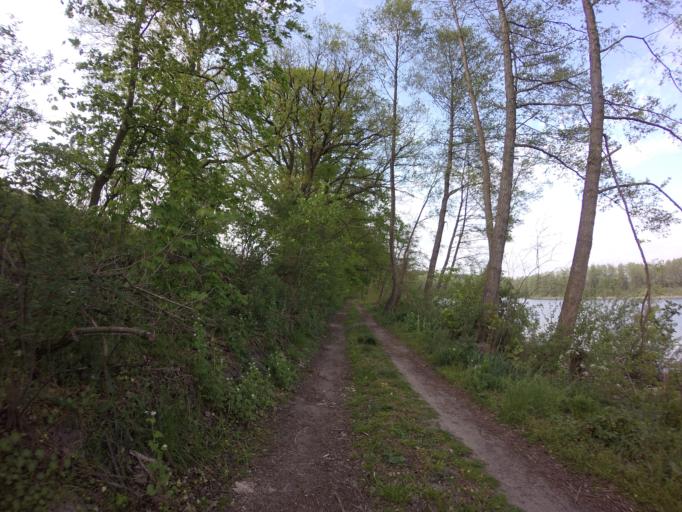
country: PL
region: West Pomeranian Voivodeship
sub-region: Powiat choszczenski
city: Choszczno
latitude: 53.1435
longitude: 15.3323
